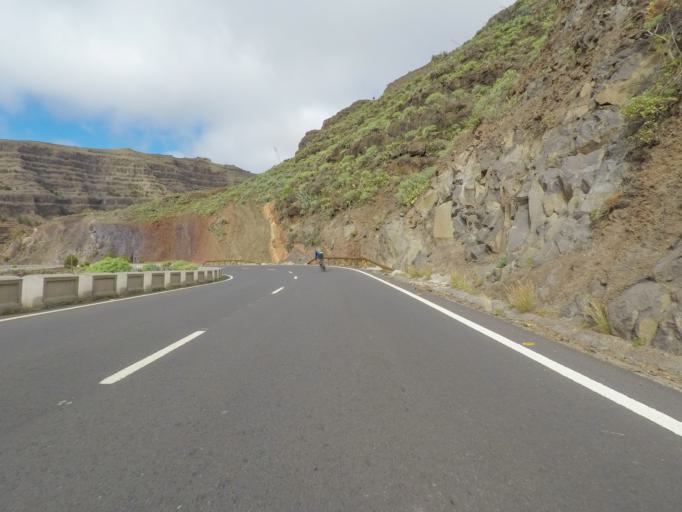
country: ES
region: Canary Islands
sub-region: Provincia de Santa Cruz de Tenerife
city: Vallehermosa
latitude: 28.1169
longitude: -17.3208
